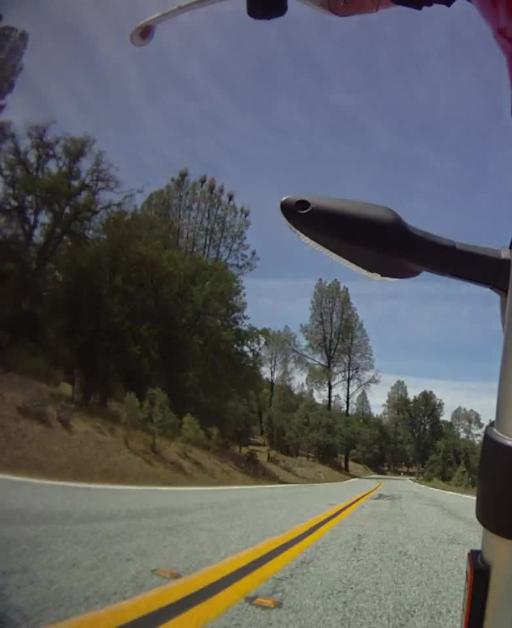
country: US
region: California
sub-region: Santa Clara County
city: Morgan Hill
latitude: 37.3396
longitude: -121.4771
